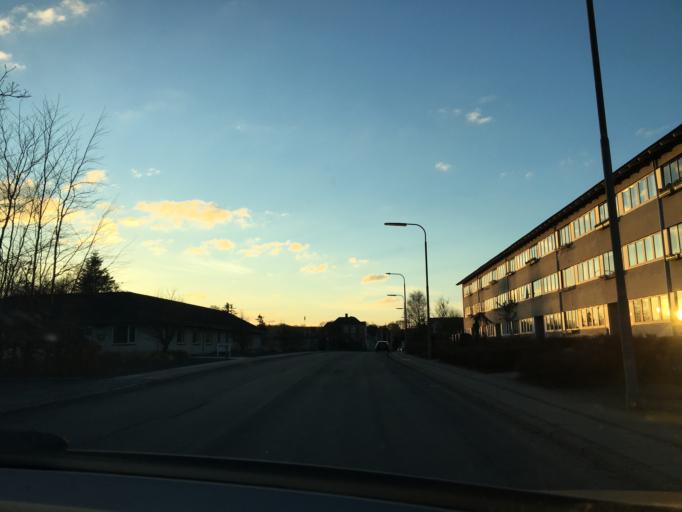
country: DK
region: South Denmark
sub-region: Middelfart Kommune
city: Middelfart
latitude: 55.5023
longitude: 9.7322
